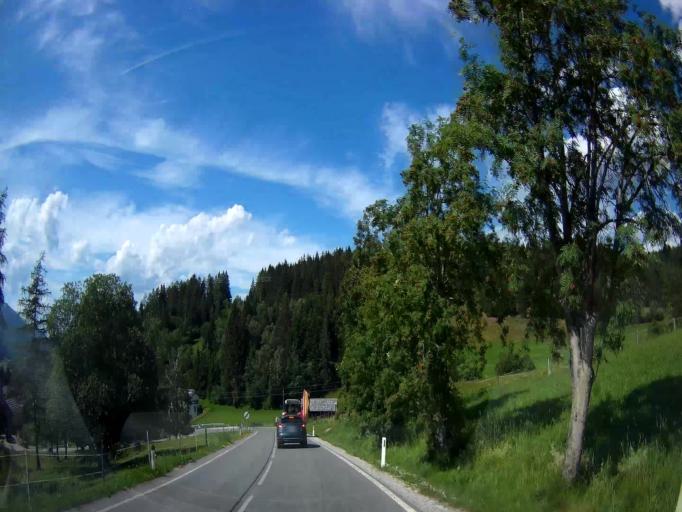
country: AT
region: Salzburg
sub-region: Politischer Bezirk Tamsweg
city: Thomatal
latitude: 47.0837
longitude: 13.7238
